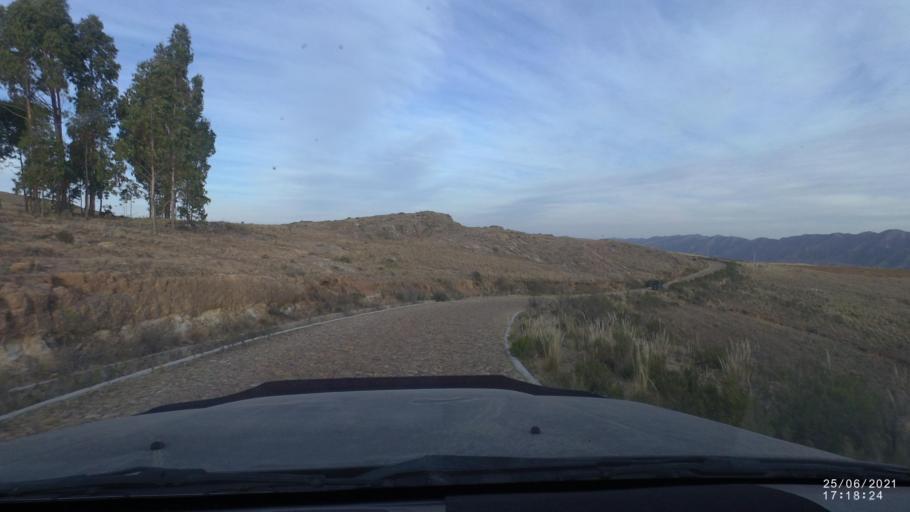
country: BO
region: Cochabamba
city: Arani
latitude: -17.8937
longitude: -65.6947
